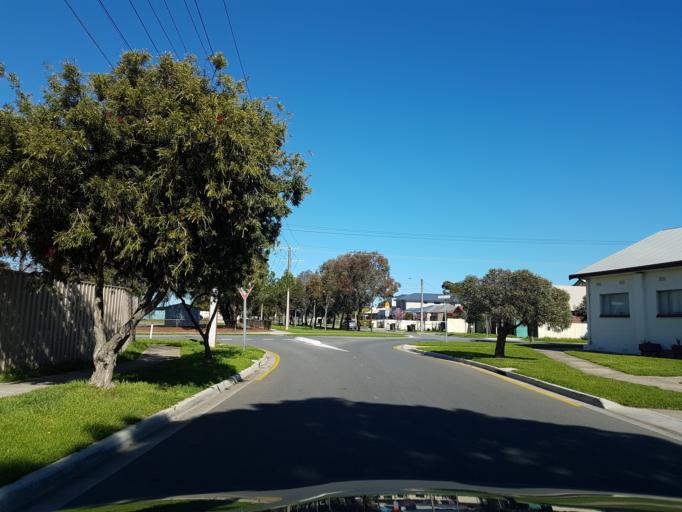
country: AU
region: South Australia
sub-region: Charles Sturt
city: Seaton
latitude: -34.8953
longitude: 138.5188
